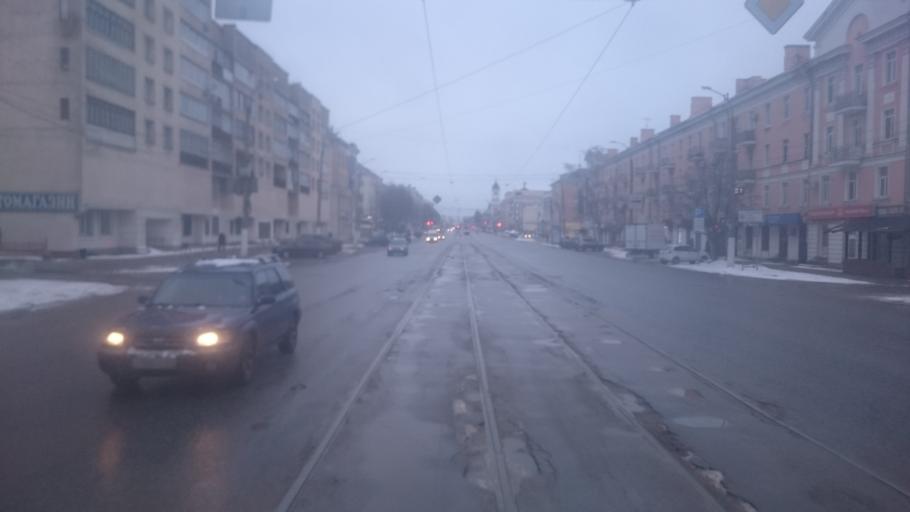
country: RU
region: Tverskaya
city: Tver
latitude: 56.8561
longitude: 35.9071
